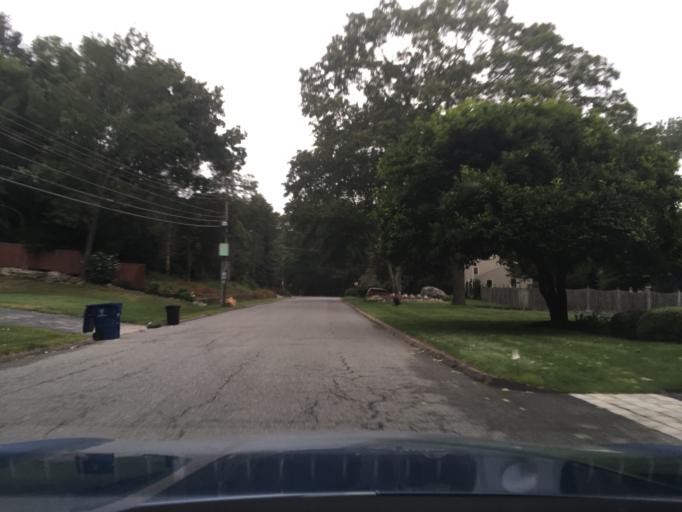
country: US
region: Rhode Island
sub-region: Kent County
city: East Greenwich
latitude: 41.6455
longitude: -71.4804
